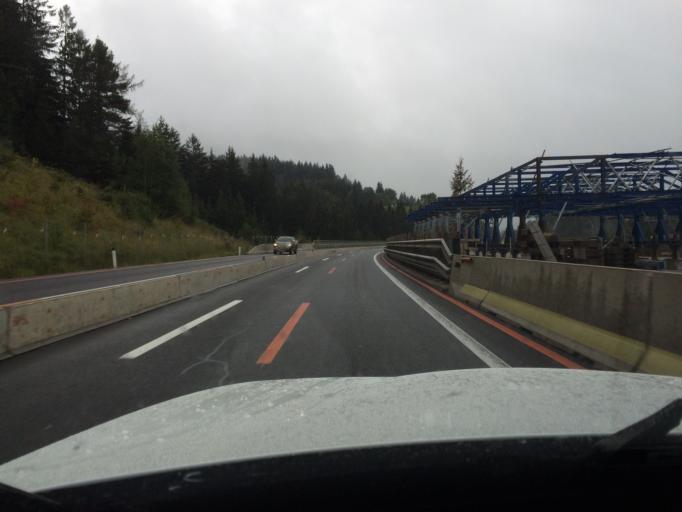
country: AT
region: Styria
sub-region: Politischer Bezirk Voitsberg
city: Voitsberg
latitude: 46.9854
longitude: 15.1220
